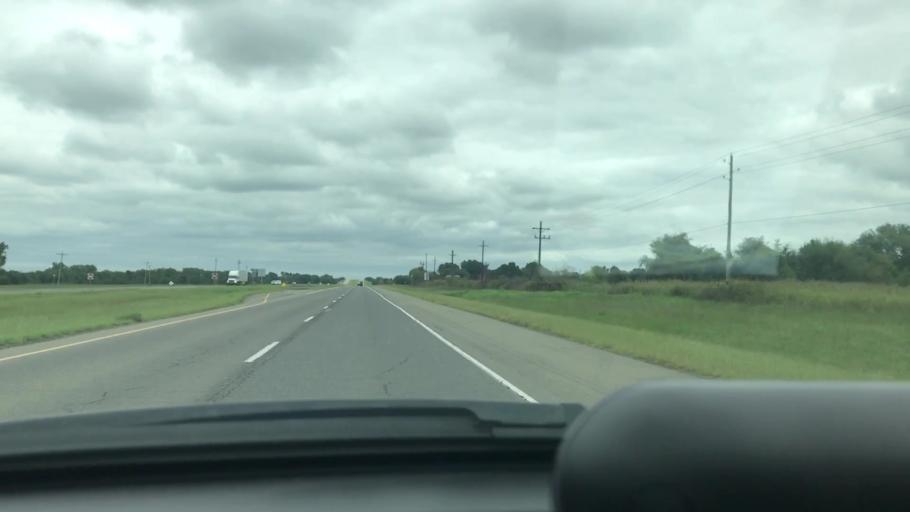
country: US
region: Oklahoma
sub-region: Wagoner County
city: Wagoner
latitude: 35.8629
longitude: -95.4026
